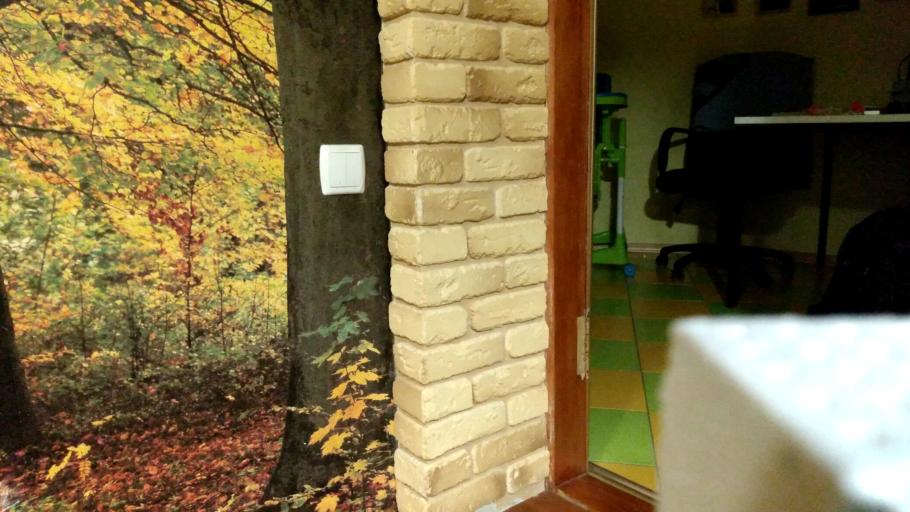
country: RU
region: Arkhangelskaya
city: Kargopol'
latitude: 61.5507
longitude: 37.7619
